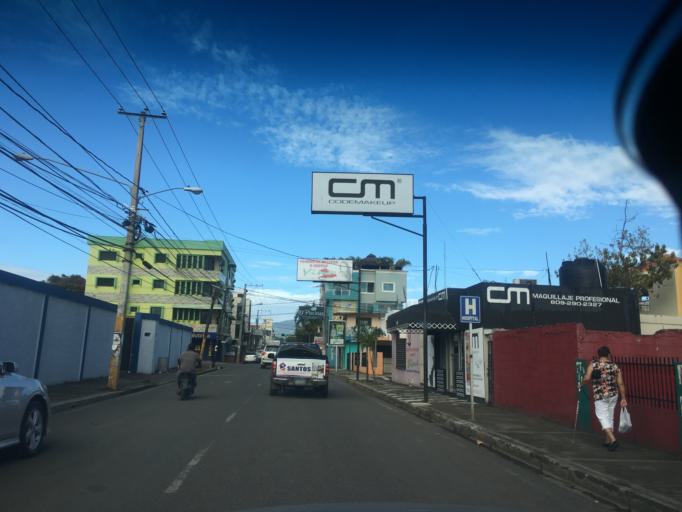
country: DO
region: Duarte
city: San Francisco de Macoris
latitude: 19.2914
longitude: -70.2601
